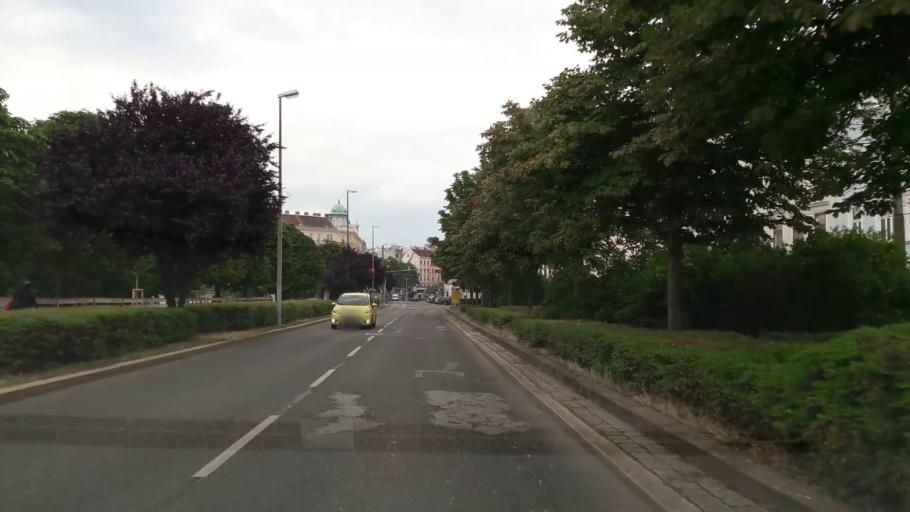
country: AT
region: Vienna
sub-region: Wien Stadt
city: Vienna
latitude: 48.2210
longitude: 16.3779
